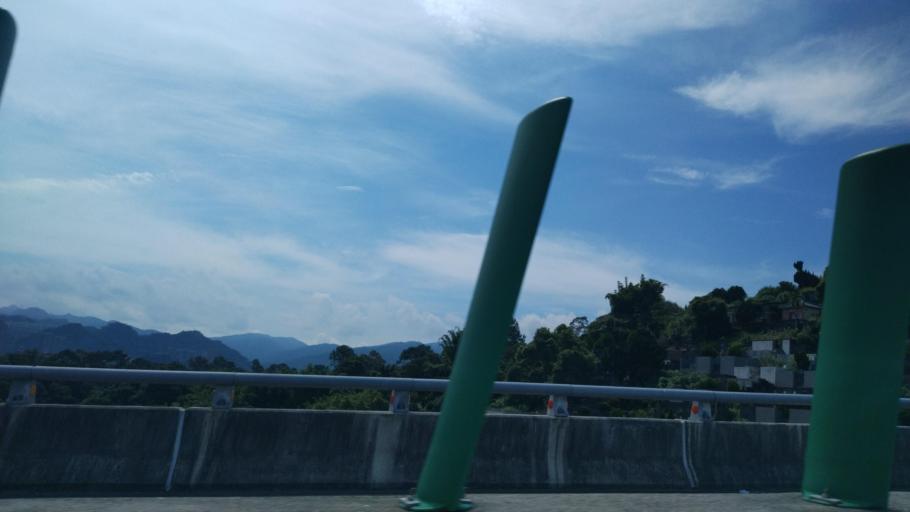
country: TW
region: Taipei
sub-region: Taipei
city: Banqiao
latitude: 24.9598
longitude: 121.5146
